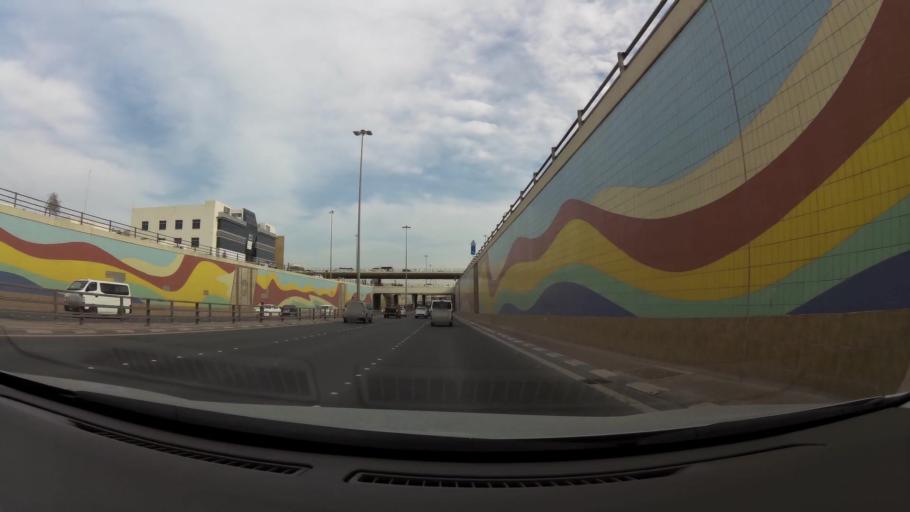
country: QA
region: Baladiyat ad Dawhah
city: Doha
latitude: 25.2654
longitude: 51.4960
